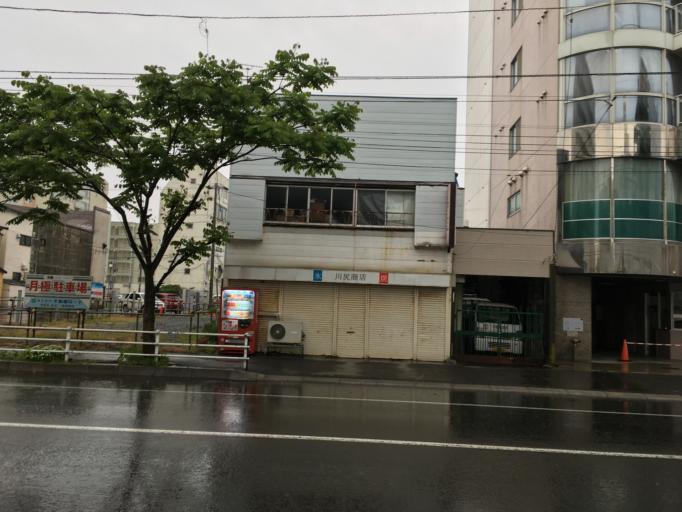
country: JP
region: Hokkaido
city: Hakodate
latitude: 41.7730
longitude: 140.7303
